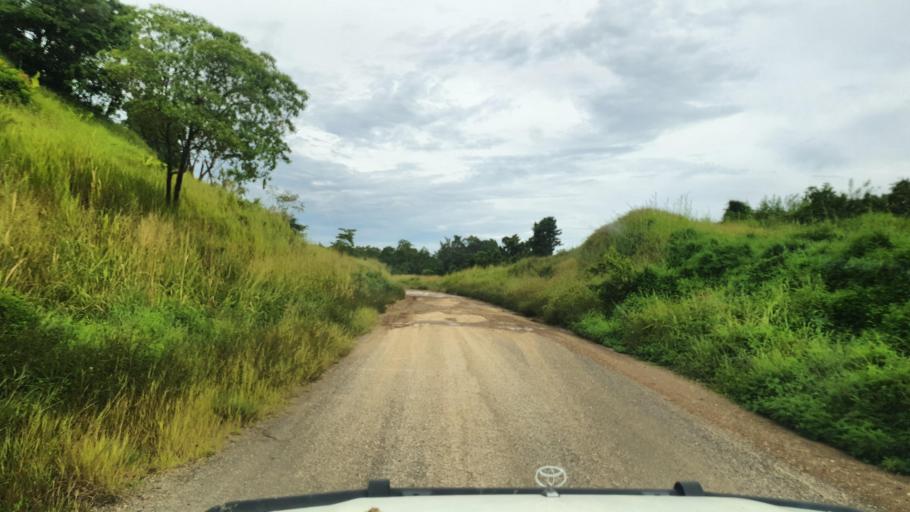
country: PG
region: Gulf
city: Kerema
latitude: -8.3338
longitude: 146.3180
